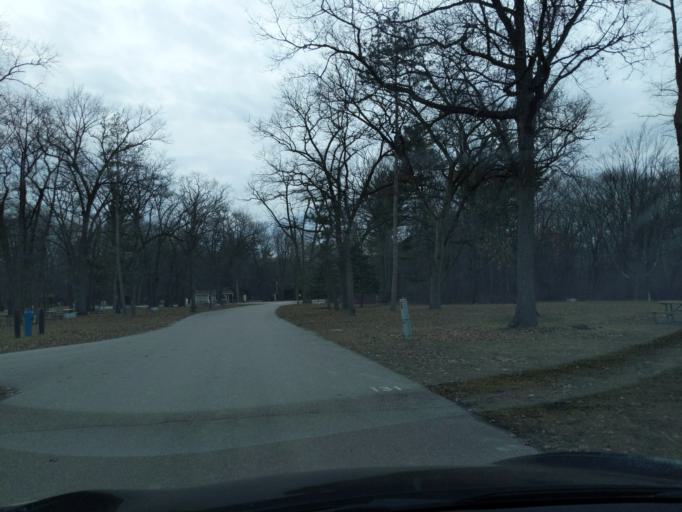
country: US
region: Michigan
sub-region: Bay County
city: Bay City
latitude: 43.6656
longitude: -83.9040
